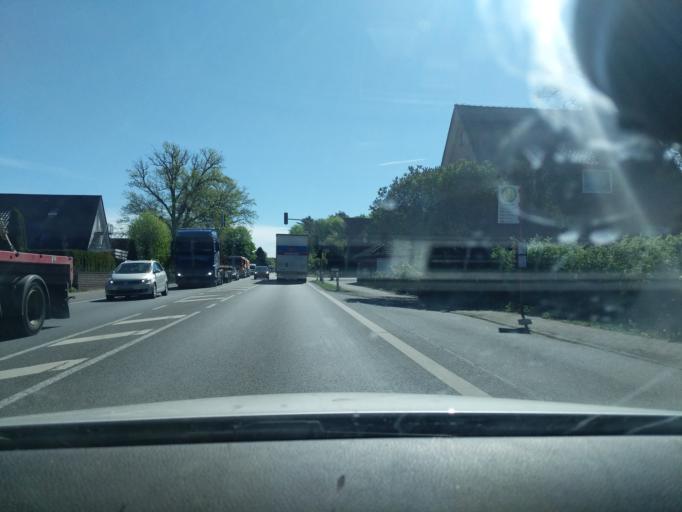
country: DE
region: Lower Saxony
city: Buxtehude
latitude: 53.4530
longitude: 9.7396
